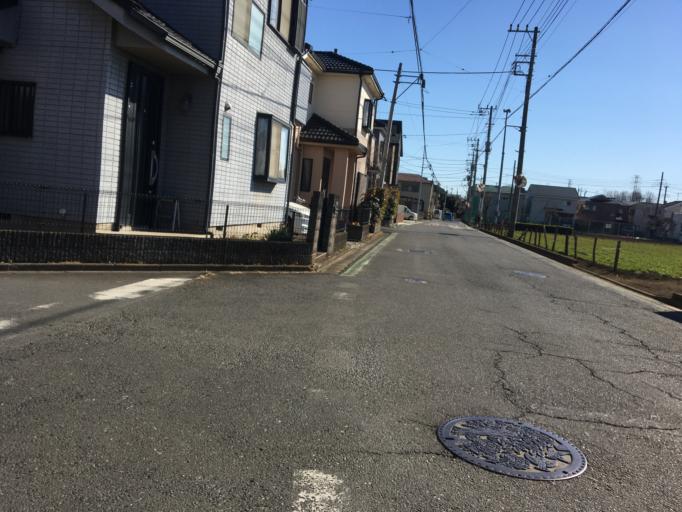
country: JP
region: Saitama
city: Oi
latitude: 35.8407
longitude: 139.5182
